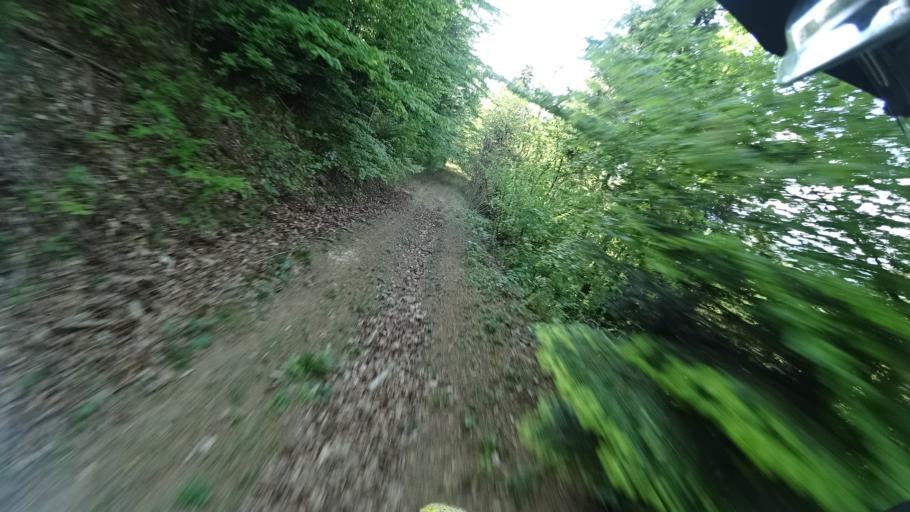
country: HR
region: Grad Zagreb
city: Kasina
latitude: 45.9472
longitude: 15.9810
